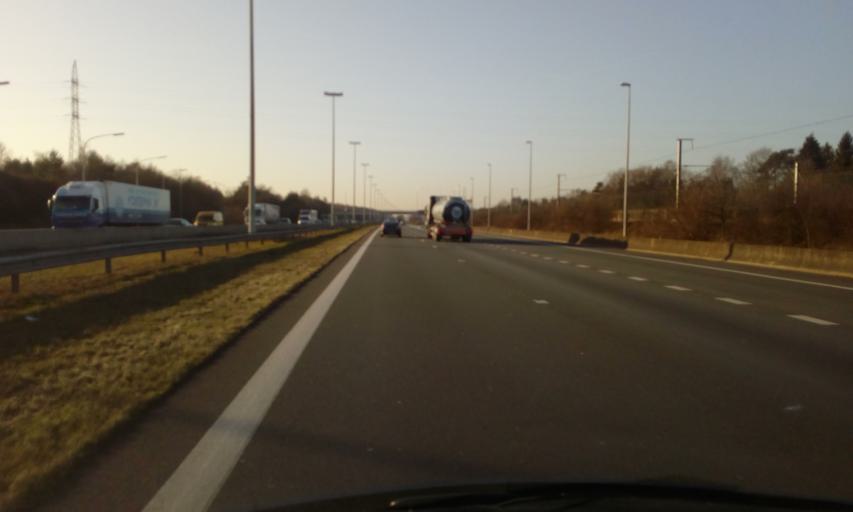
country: BE
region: Flanders
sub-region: Provincie Antwerpen
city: Schilde
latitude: 51.3117
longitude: 4.5630
